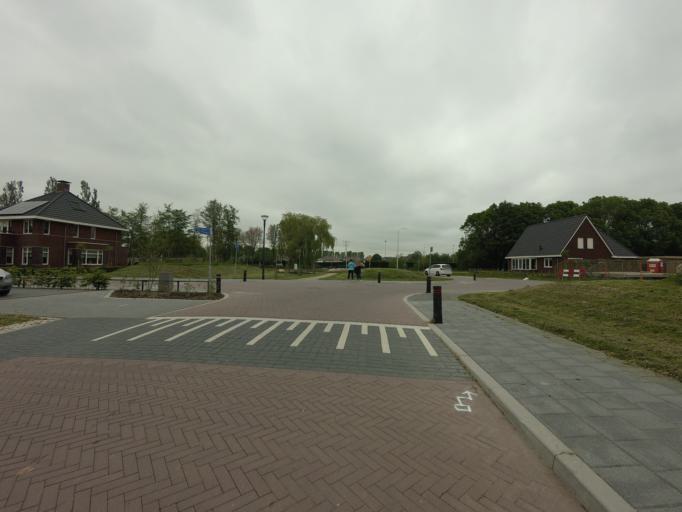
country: NL
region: South Holland
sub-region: Gemeente Spijkenisse
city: Spijkenisse
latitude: 51.8068
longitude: 4.3444
